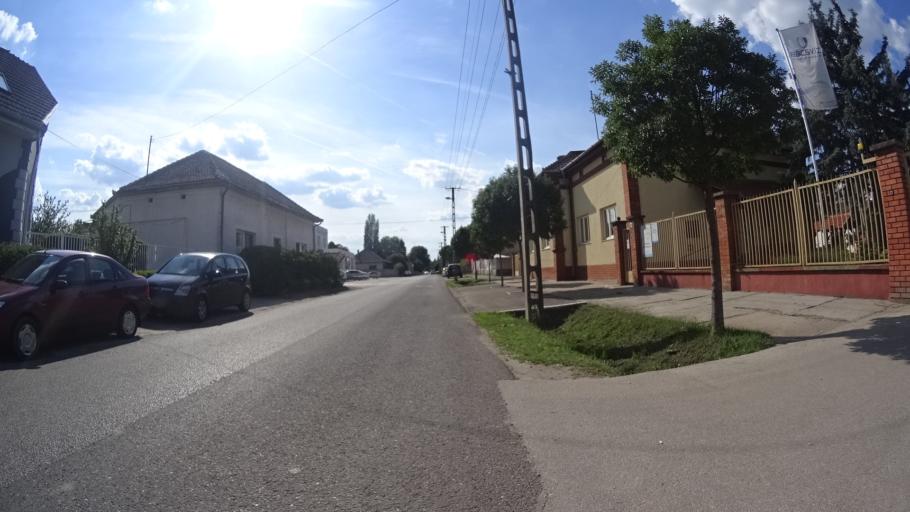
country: HU
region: Bacs-Kiskun
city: Tiszakecske
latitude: 46.9290
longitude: 20.1072
